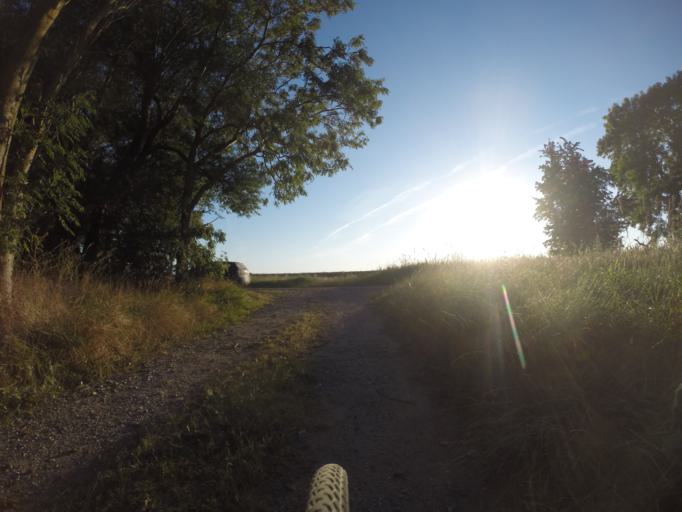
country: DK
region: Capital Region
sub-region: Egedal Kommune
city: Smorumnedre
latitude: 55.7000
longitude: 12.3134
